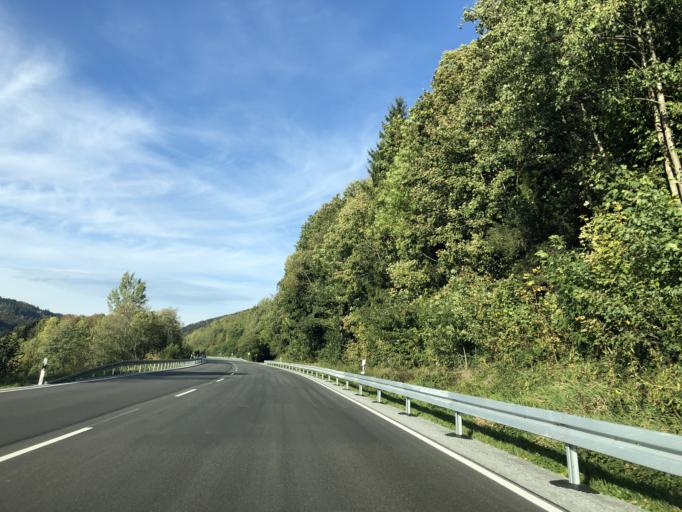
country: DE
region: Bavaria
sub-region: Lower Bavaria
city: Grafling
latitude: 48.9148
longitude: 12.9804
